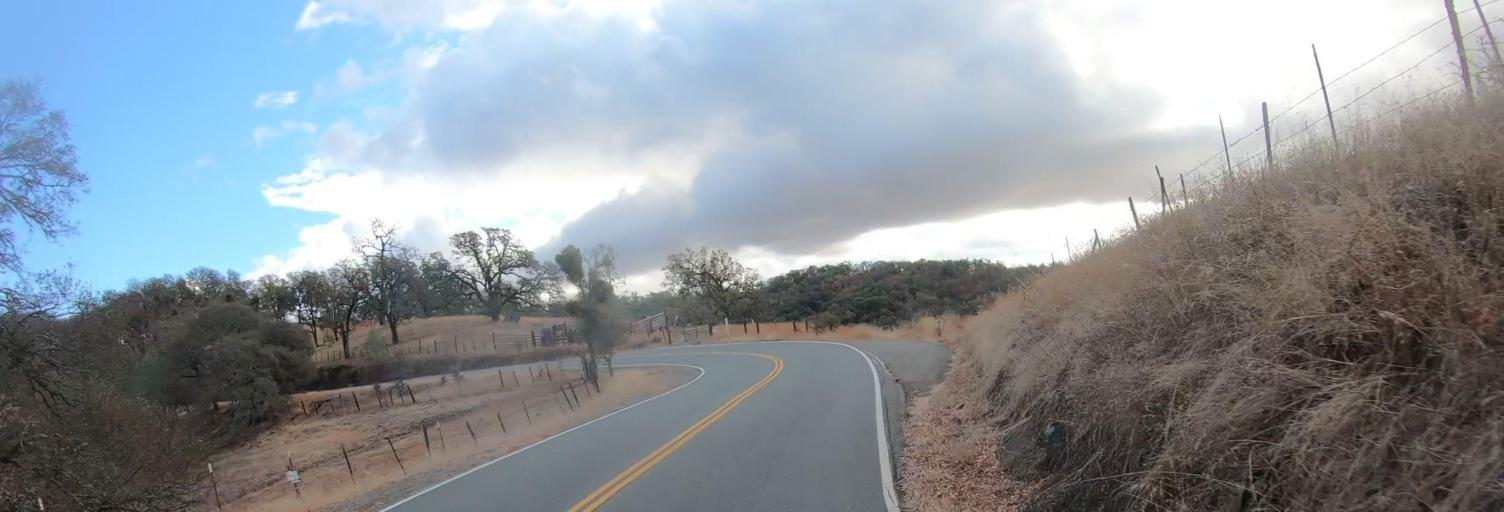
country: US
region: California
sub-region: Santa Clara County
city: East Foothills
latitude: 37.3277
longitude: -121.6683
